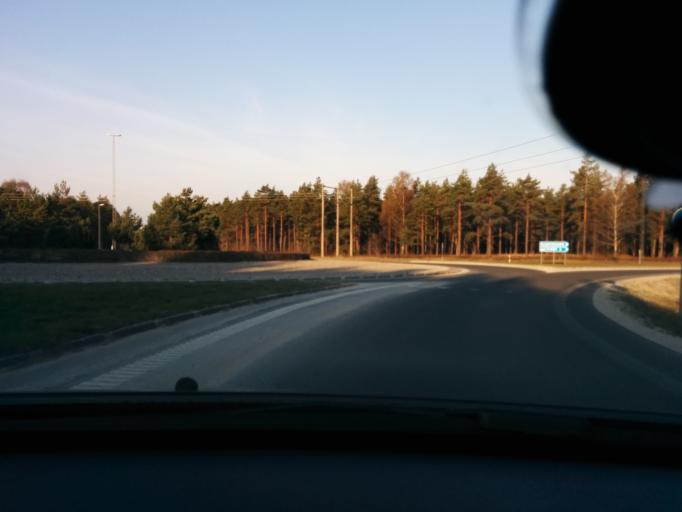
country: SE
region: Gotland
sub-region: Gotland
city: Visby
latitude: 57.6088
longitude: 18.3003
